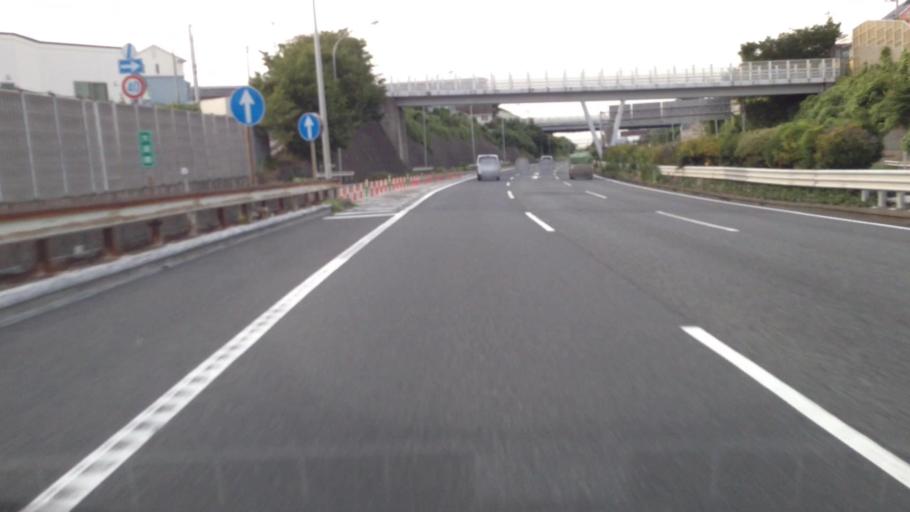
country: JP
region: Kanagawa
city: Yokohama
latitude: 35.4879
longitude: 139.5922
